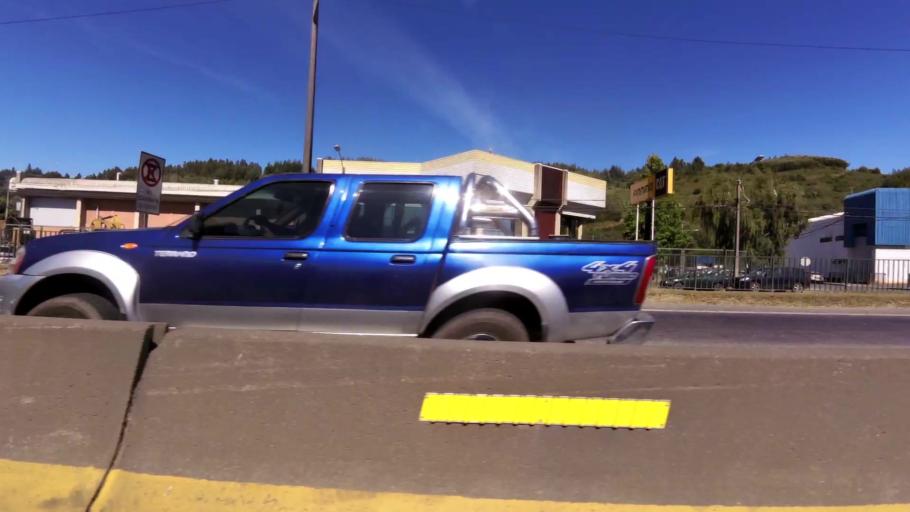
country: CL
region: Biobio
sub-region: Provincia de Concepcion
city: Concepcion
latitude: -36.8076
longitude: -73.0244
